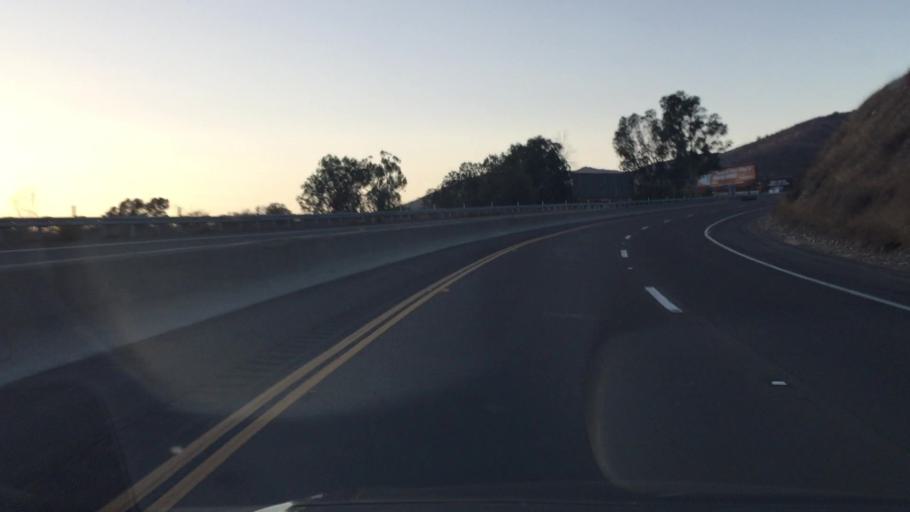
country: US
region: California
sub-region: San Diego County
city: Eucalyptus Hills
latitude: 32.9094
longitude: -116.9466
